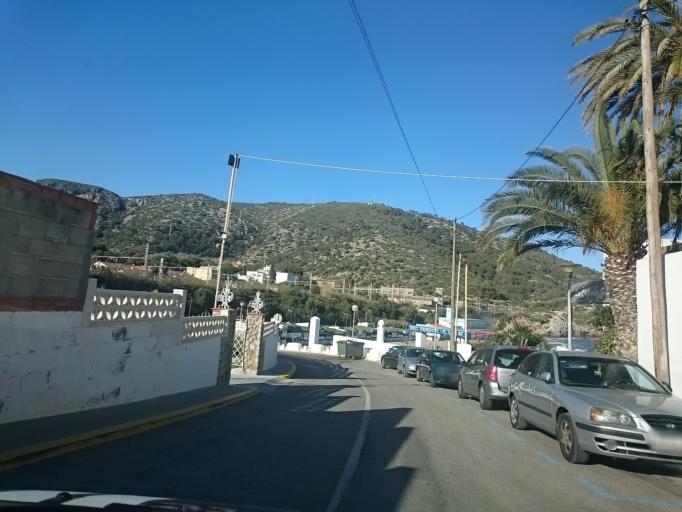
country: ES
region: Catalonia
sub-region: Provincia de Barcelona
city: Castelldefels
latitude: 41.2531
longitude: 1.9025
